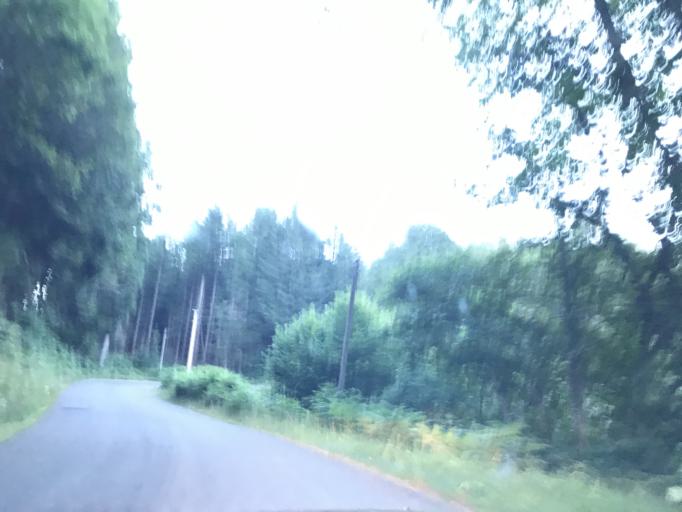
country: FR
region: Rhone-Alpes
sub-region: Departement de la Loire
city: Noiretable
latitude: 45.8125
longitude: 3.7286
